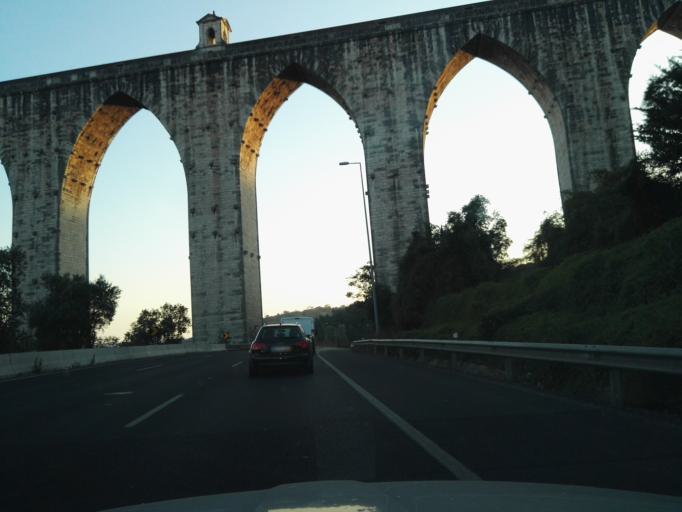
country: PT
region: Lisbon
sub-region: Lisbon
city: Lisbon
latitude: 38.7306
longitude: -9.1701
